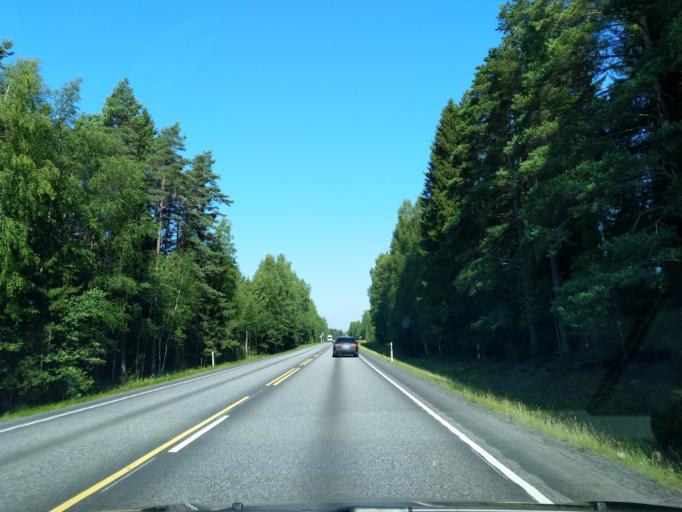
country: FI
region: Satakunta
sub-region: Pori
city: Huittinen
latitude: 61.1413
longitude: 22.7608
